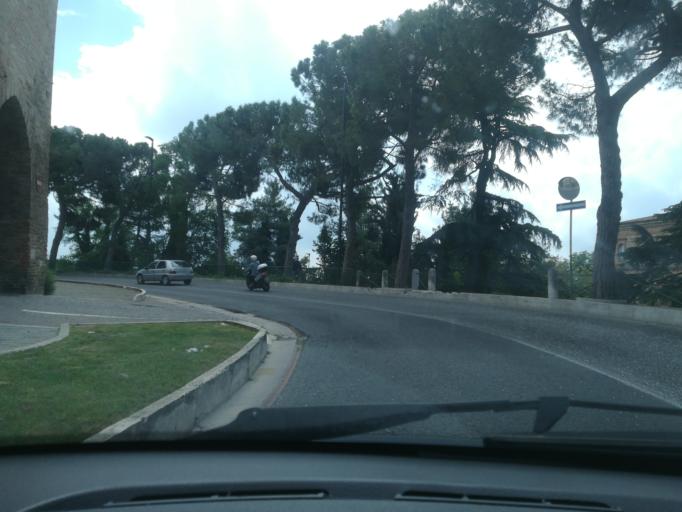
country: IT
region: The Marches
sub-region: Provincia di Macerata
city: Macerata
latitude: 43.2979
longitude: 13.4489
